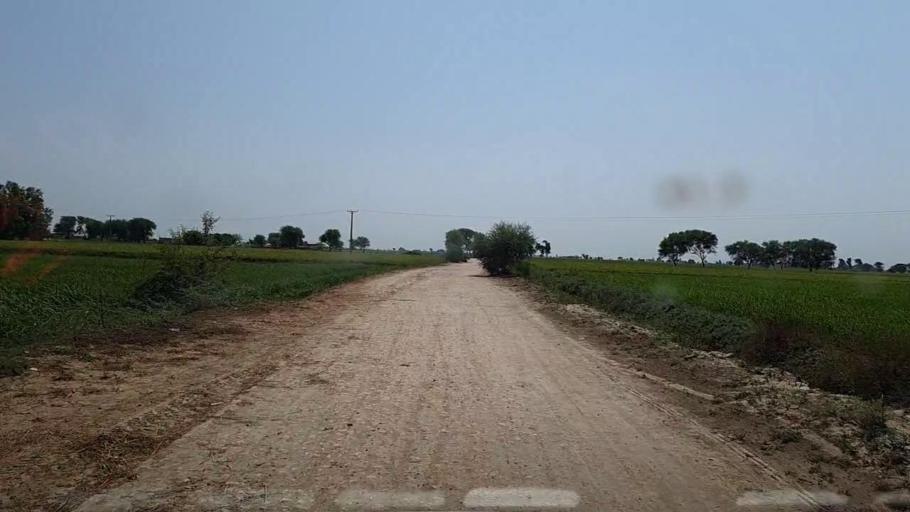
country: PK
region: Sindh
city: Kario
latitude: 24.6394
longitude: 68.4870
